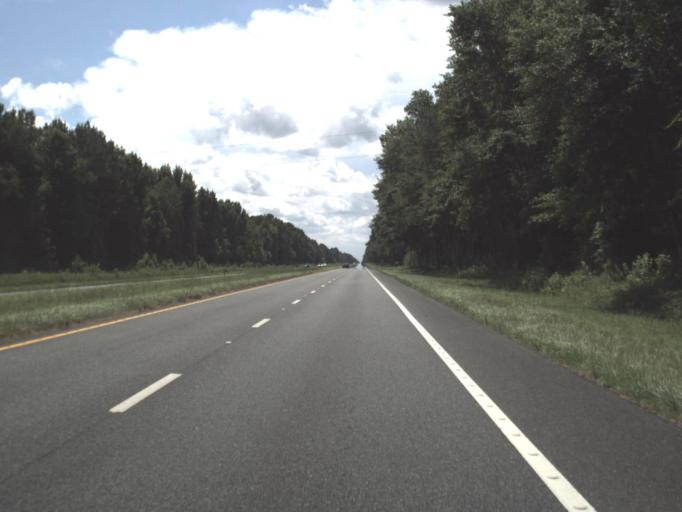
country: US
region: Florida
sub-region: Taylor County
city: Perry
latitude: 30.2774
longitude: -83.7248
